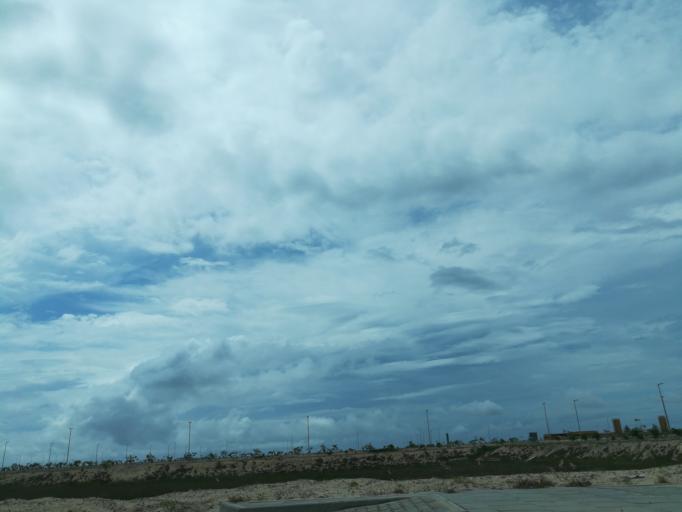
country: NG
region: Lagos
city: Lagos
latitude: 6.4091
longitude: 3.4129
